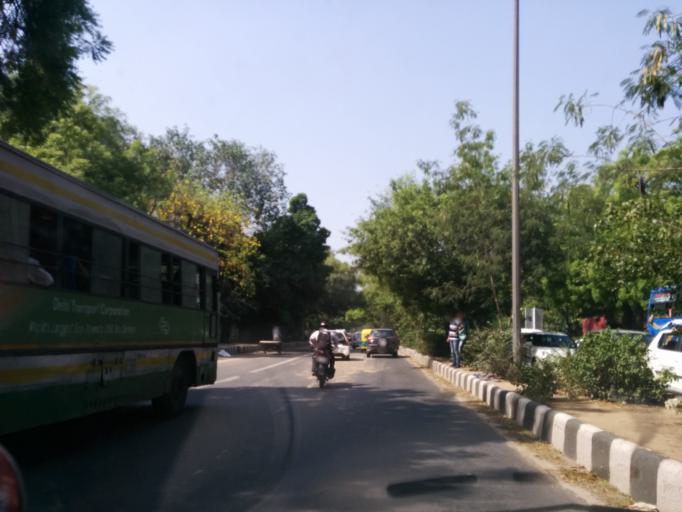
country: IN
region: NCT
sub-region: New Delhi
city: New Delhi
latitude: 28.5429
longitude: 77.2006
